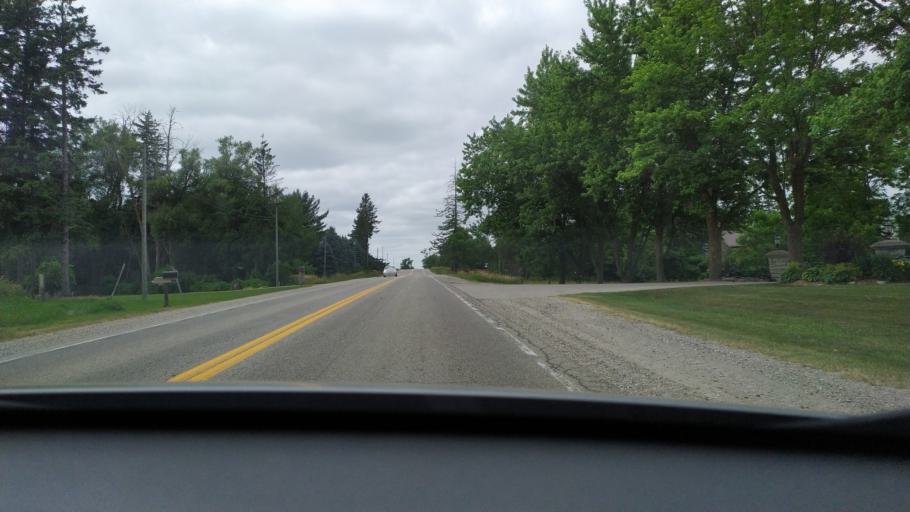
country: CA
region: Ontario
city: Stratford
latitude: 43.3018
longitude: -80.9764
